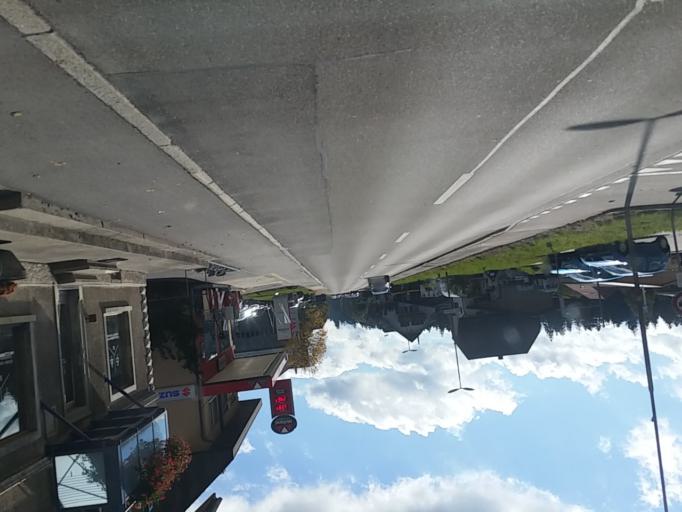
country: CH
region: Bern
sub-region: Emmental District
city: Sumiswald
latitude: 47.0629
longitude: 7.7493
